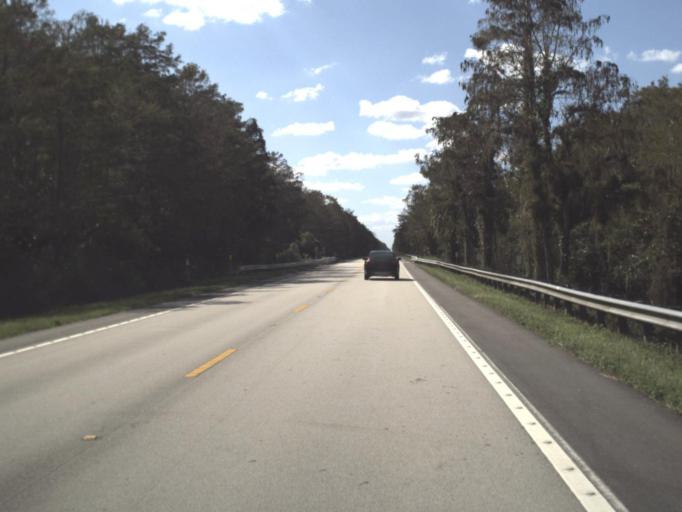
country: US
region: Florida
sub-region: Miami-Dade County
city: Kendall West
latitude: 25.8535
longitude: -80.9999
